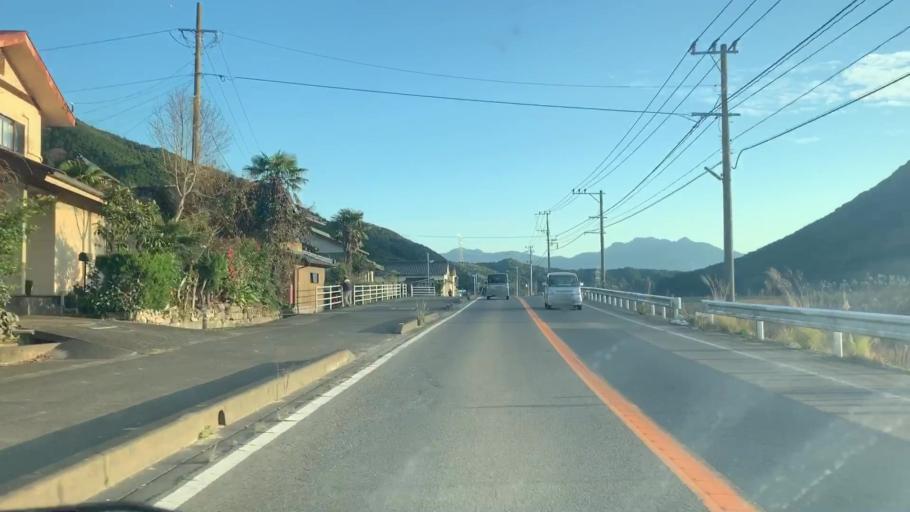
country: JP
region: Saga Prefecture
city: Karatsu
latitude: 33.3724
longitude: 130.0026
